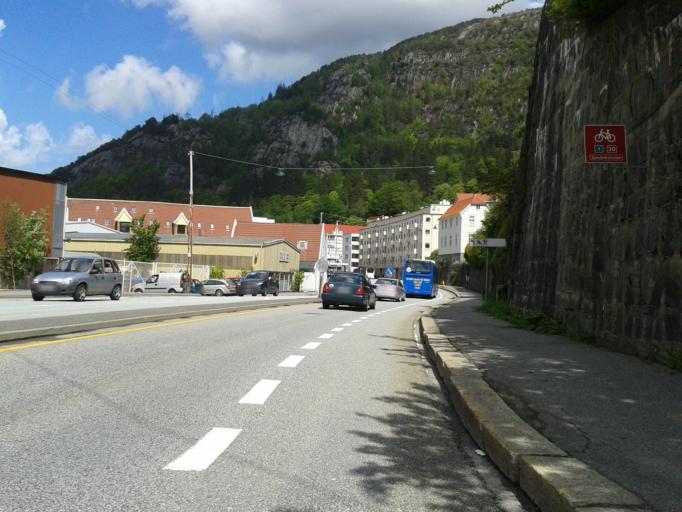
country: NO
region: Hordaland
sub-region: Bergen
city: Bergen
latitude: 60.4096
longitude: 5.3227
